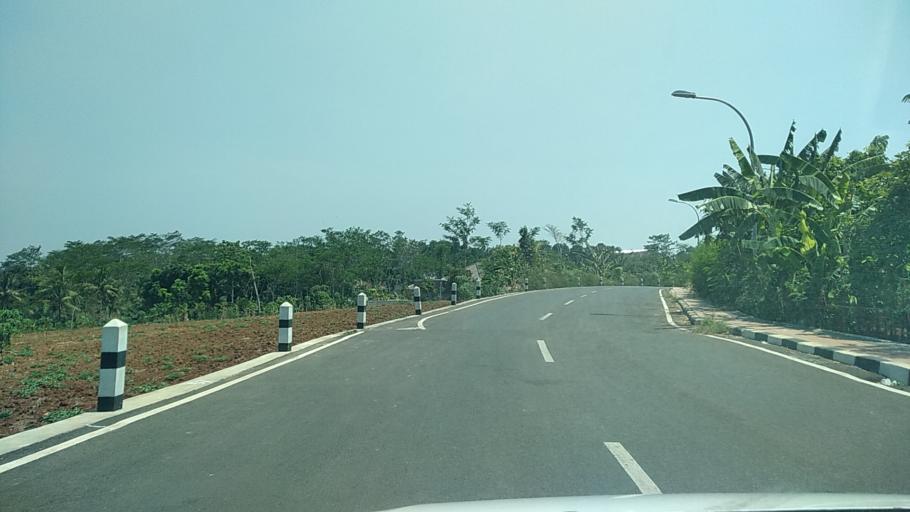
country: ID
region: Central Java
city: Ungaran
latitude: -7.0850
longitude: 110.3600
